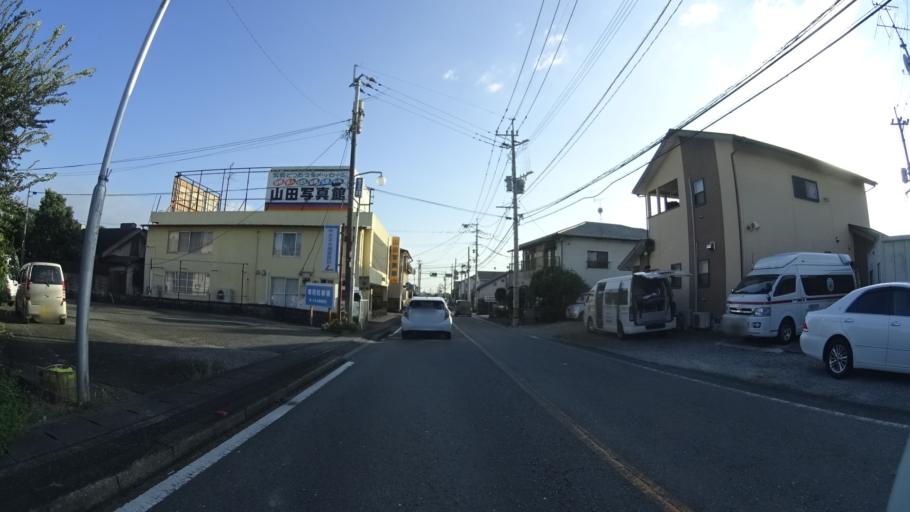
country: JP
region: Kumamoto
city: Matsubase
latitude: 32.6503
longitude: 130.6787
